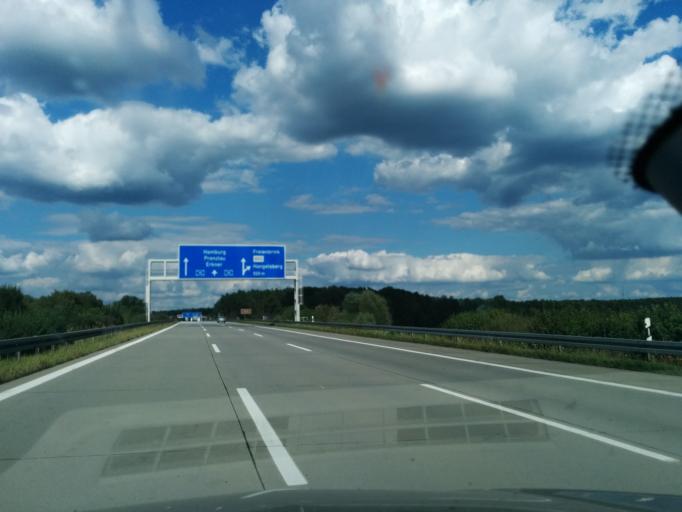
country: DE
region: Brandenburg
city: Erkner
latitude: 52.3809
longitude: 13.7792
